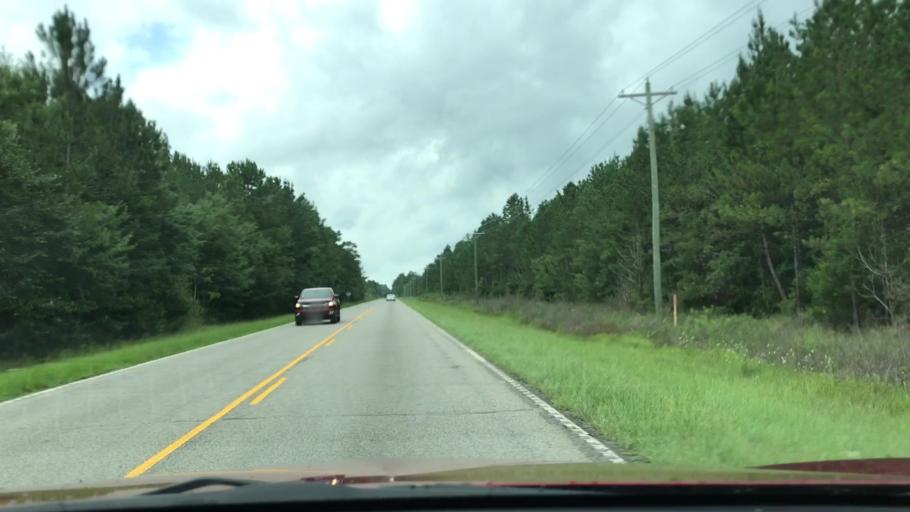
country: US
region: South Carolina
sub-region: Georgetown County
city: Murrells Inlet
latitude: 33.5749
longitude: -79.2096
